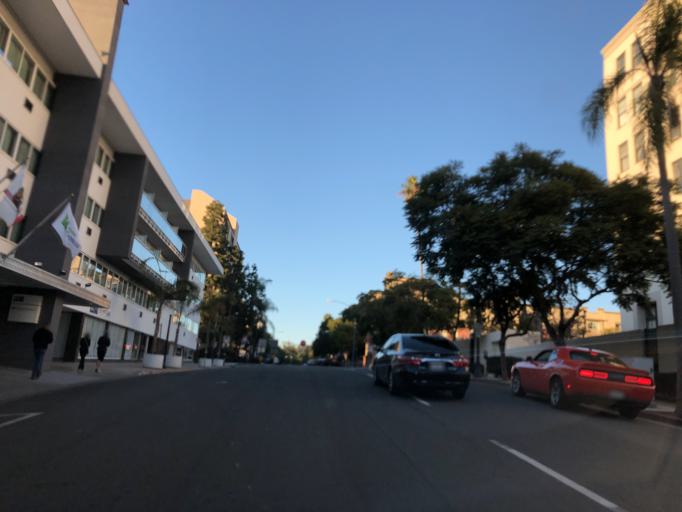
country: US
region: California
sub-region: San Diego County
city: San Diego
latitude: 32.7202
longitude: -117.1583
